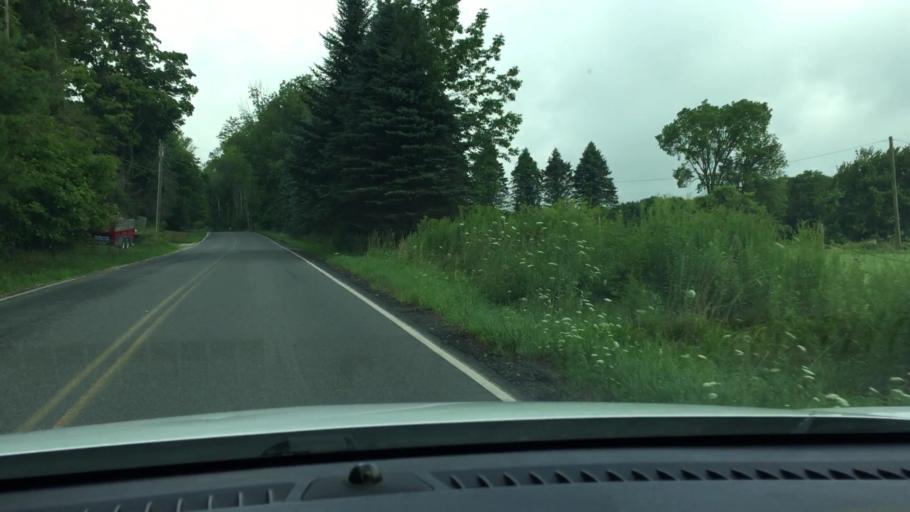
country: US
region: Massachusetts
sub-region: Berkshire County
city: Hinsdale
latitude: 42.4434
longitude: -73.1391
